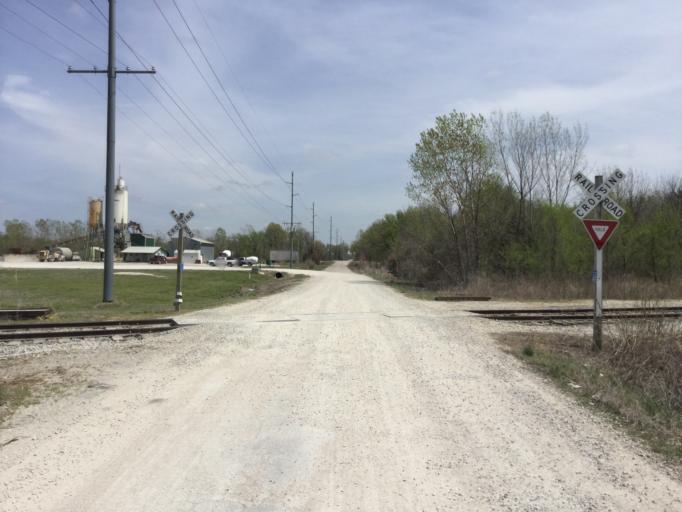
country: US
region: Kansas
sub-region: Neosho County
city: Chanute
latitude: 37.6963
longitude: -95.4511
